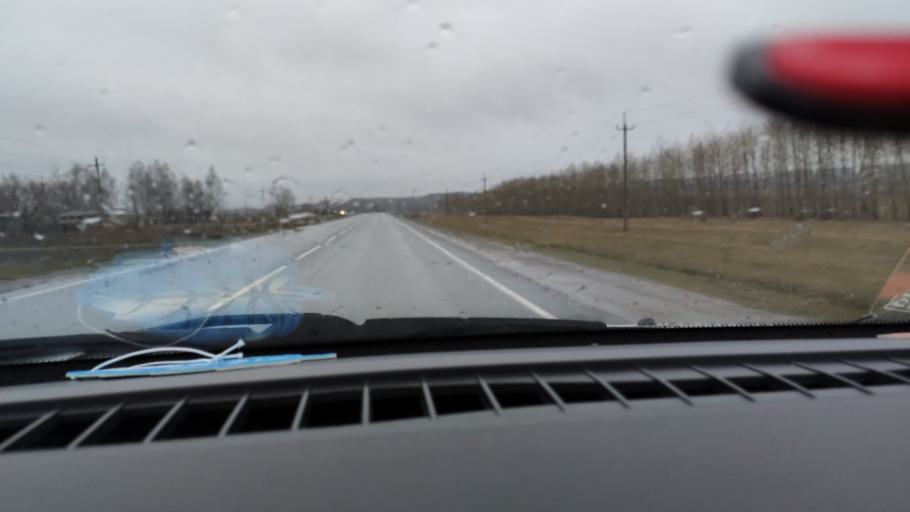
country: RU
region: Tatarstan
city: Mendeleyevsk
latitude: 55.9745
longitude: 52.3198
